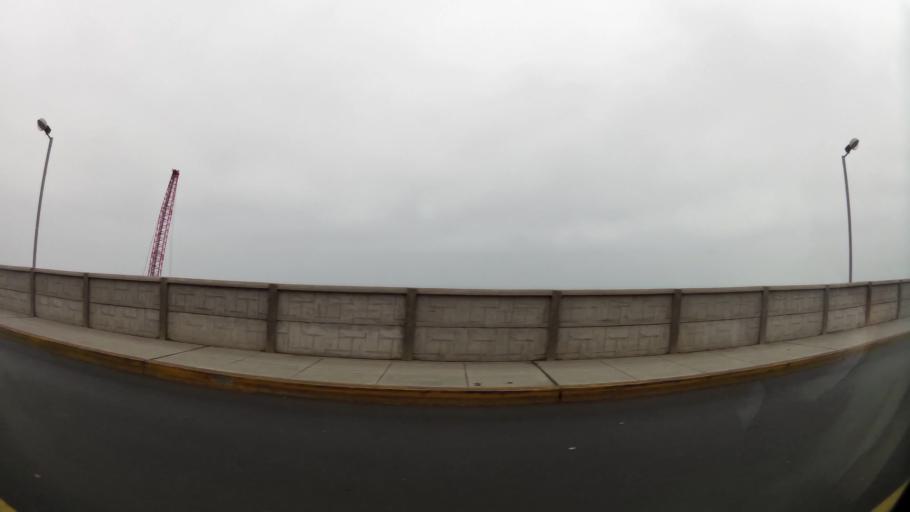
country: PE
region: Callao
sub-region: Callao
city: Callao
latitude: -12.0763
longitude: -77.1173
